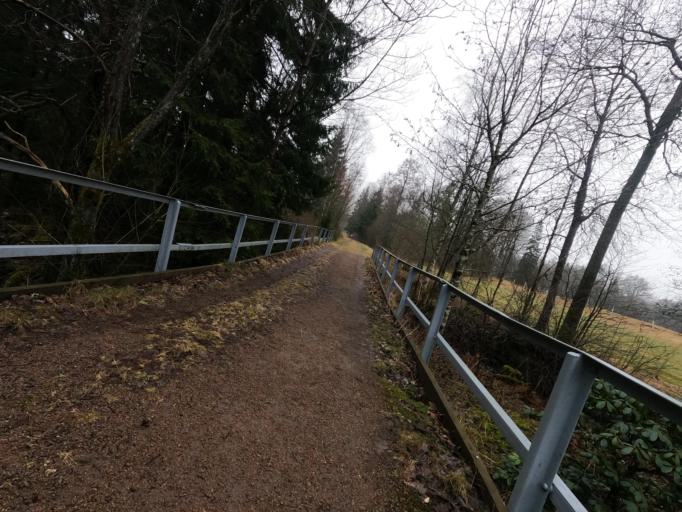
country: SE
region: Halland
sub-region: Hylte Kommun
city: Hyltebruk
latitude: 56.7994
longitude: 13.2471
